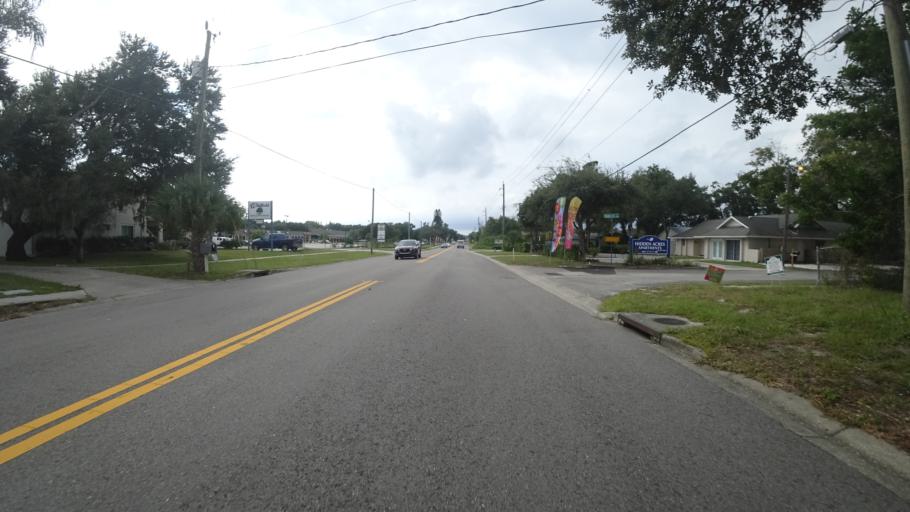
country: US
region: Florida
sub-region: Manatee County
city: Whitfield
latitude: 27.4183
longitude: -82.5491
